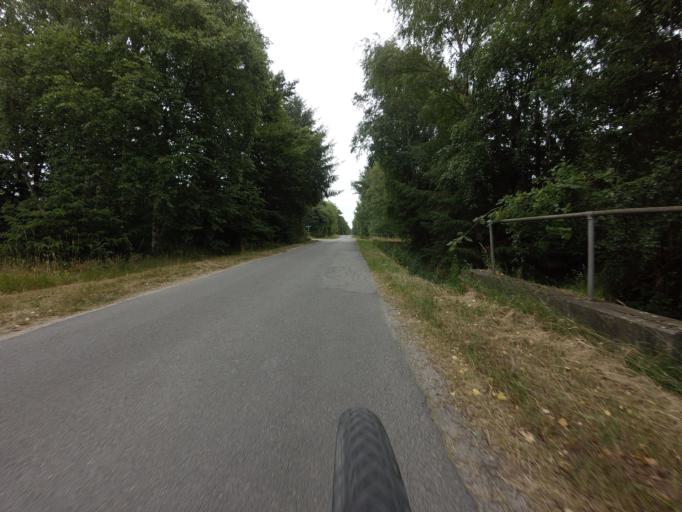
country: DK
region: North Denmark
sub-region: Laeso Kommune
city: Byrum
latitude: 57.2942
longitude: 10.9389
